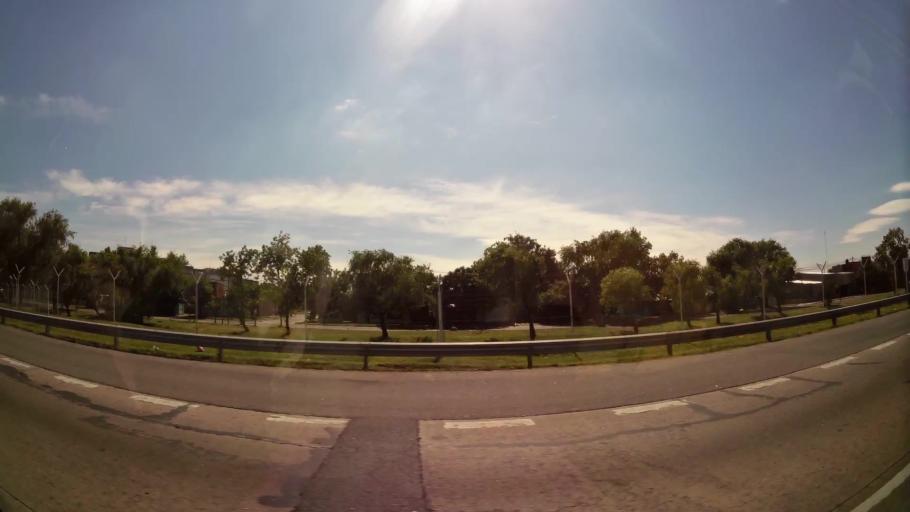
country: AR
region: Buenos Aires
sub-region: Partido de Tigre
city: Tigre
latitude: -34.4494
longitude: -58.5764
